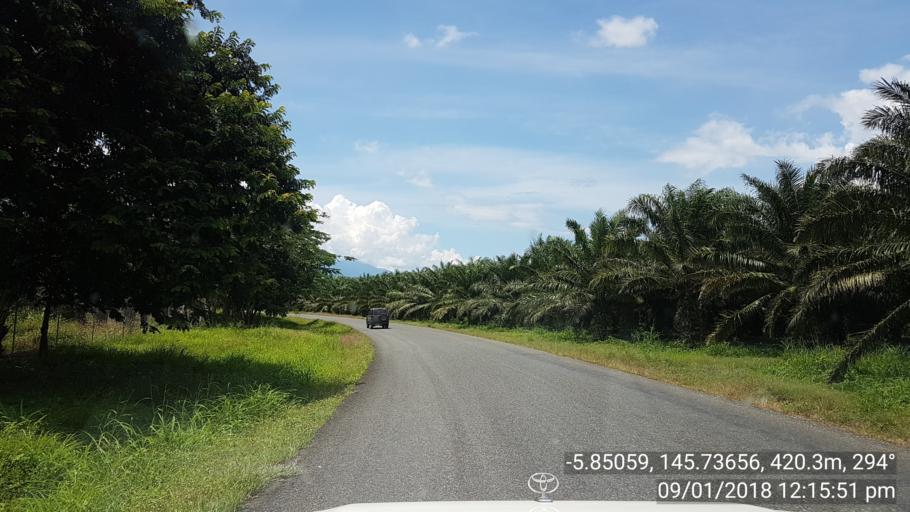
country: PG
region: Eastern Highlands
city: Goroka
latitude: -5.8506
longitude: 145.7367
